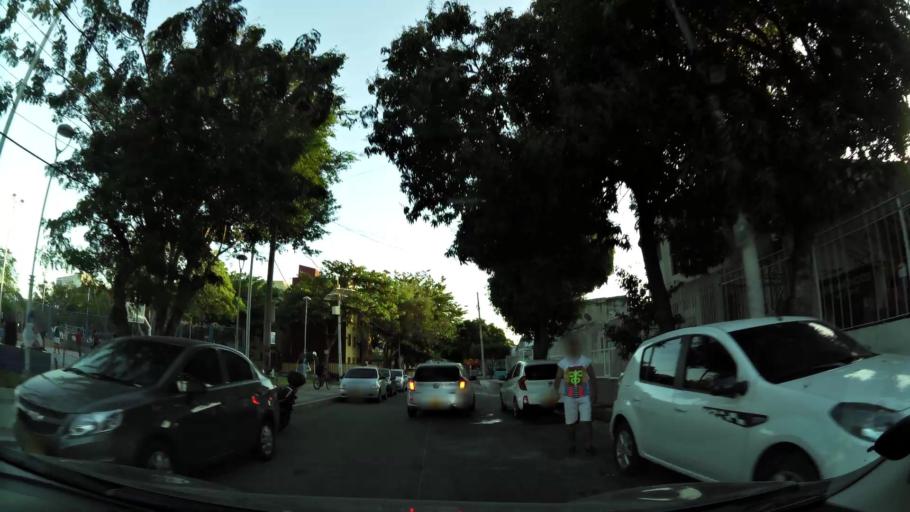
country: CO
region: Atlantico
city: Barranquilla
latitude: 10.9748
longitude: -74.8040
